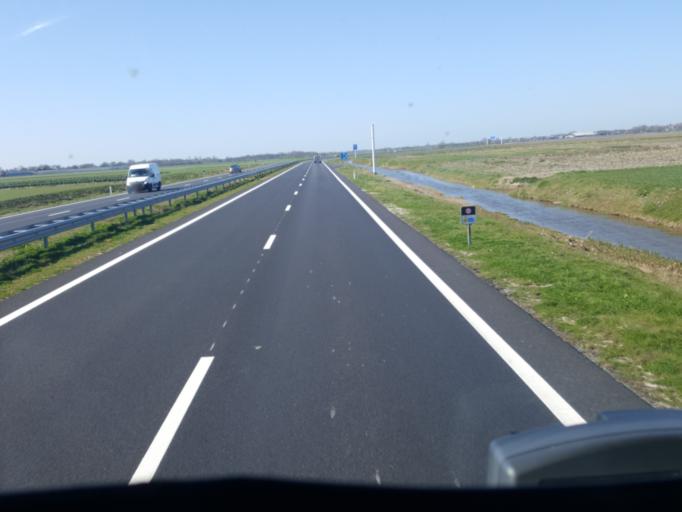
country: NL
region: North Holland
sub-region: Gemeente Enkhuizen
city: Enkhuizen
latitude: 52.6781
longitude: 5.1814
